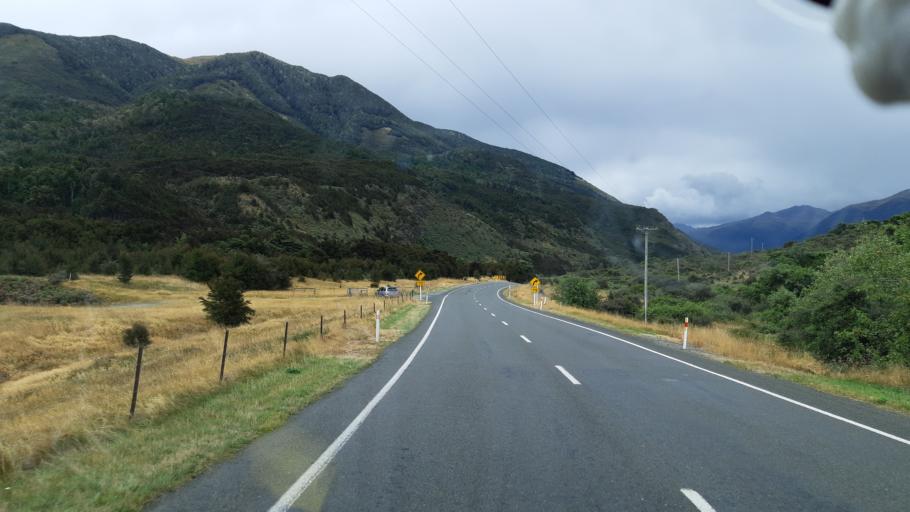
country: NZ
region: Canterbury
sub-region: Hurunui District
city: Amberley
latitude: -42.5707
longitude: 172.3648
